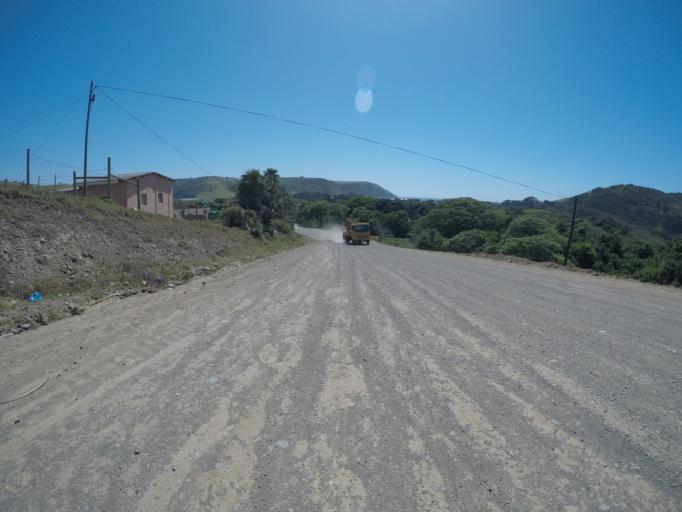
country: ZA
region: Eastern Cape
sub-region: OR Tambo District Municipality
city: Libode
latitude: -31.9869
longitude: 29.1477
